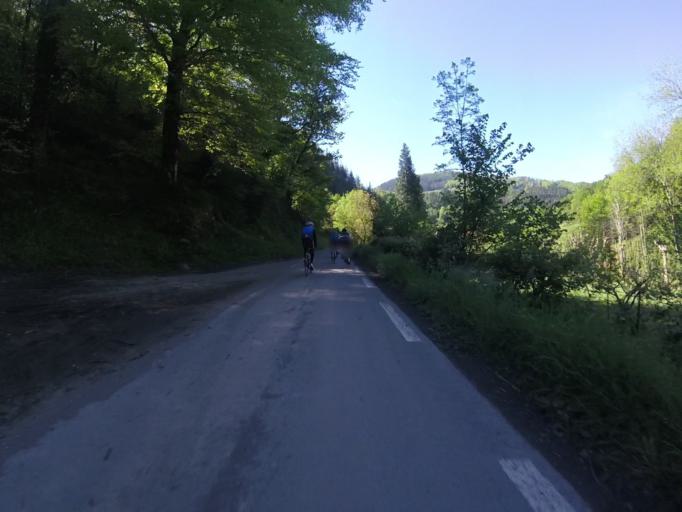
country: ES
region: Basque Country
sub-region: Provincia de Guipuzcoa
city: Errezil
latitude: 43.1783
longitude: -2.2040
